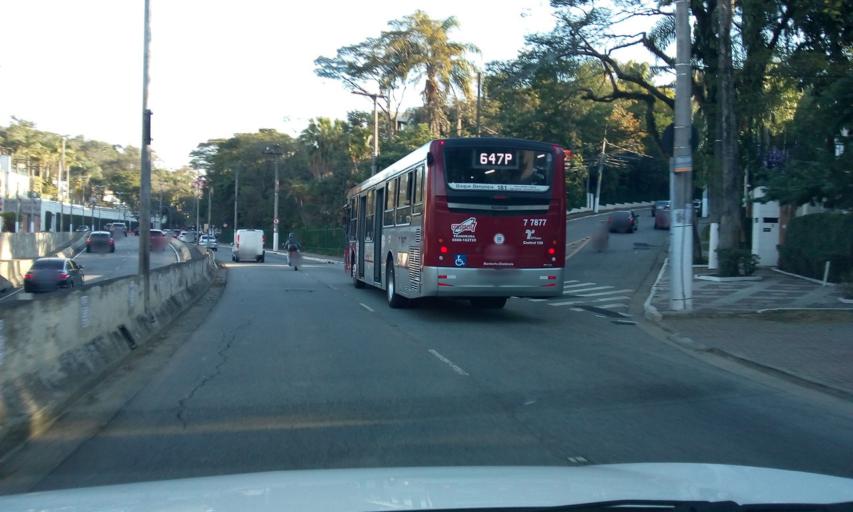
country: BR
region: Sao Paulo
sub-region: Sao Paulo
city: Sao Paulo
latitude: -23.5868
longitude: -46.6988
